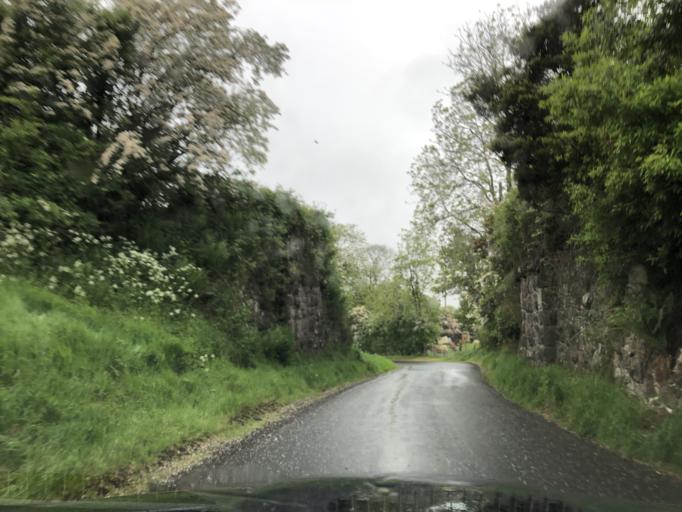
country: GB
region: Northern Ireland
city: Dunloy
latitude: 55.1361
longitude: -6.3708
